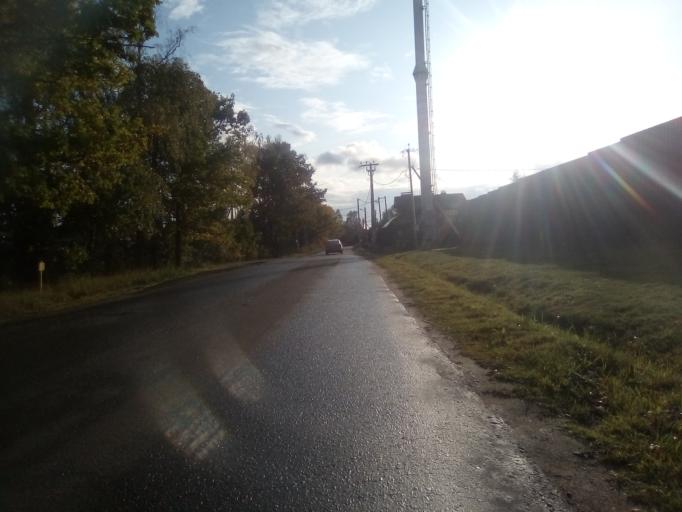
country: RU
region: Moskovskaya
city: Krasnoznamensk
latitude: 55.5705
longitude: 37.0181
